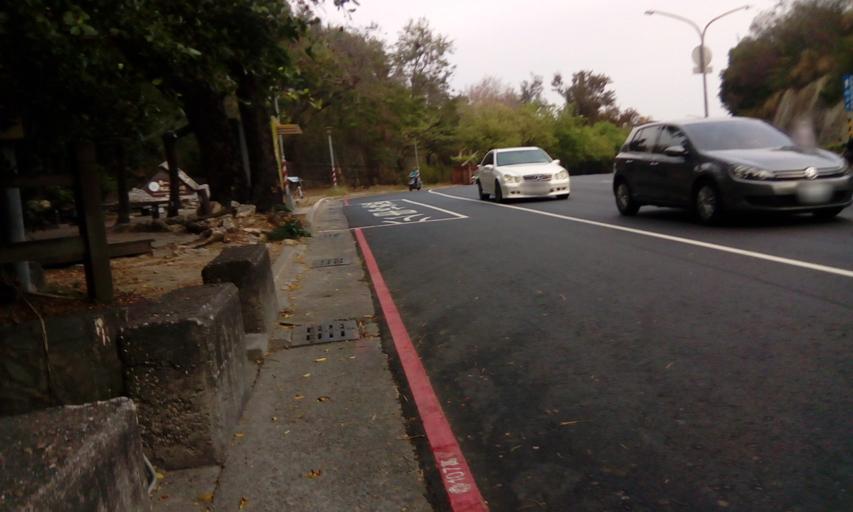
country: TW
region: Kaohsiung
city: Kaohsiung
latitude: 22.6800
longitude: 120.2919
